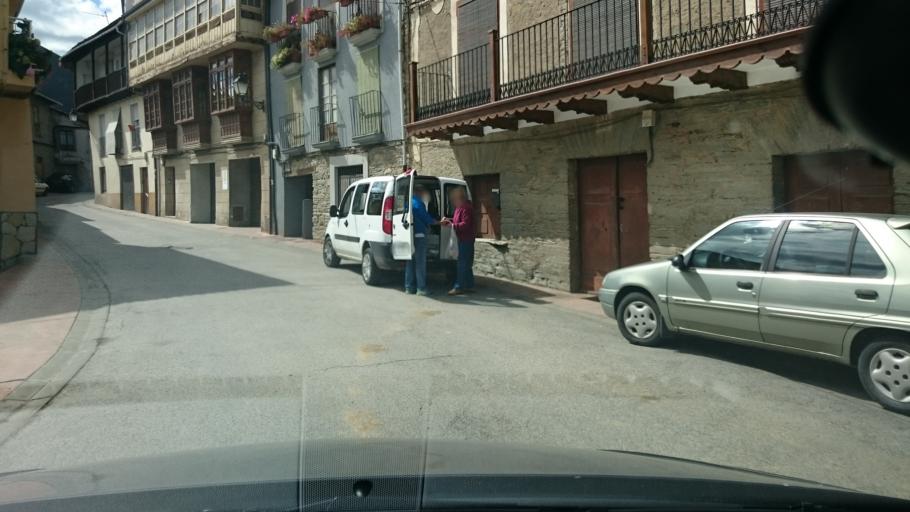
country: ES
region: Castille and Leon
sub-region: Provincia de Leon
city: Villafranca del Bierzo
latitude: 42.6096
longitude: -6.8142
